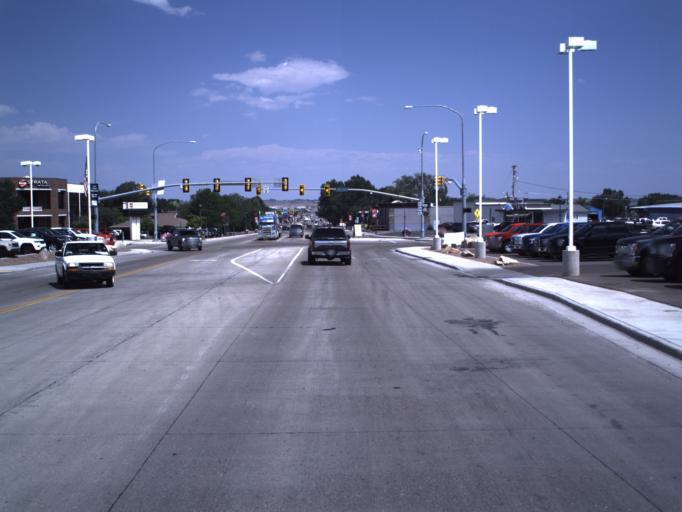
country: US
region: Utah
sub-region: Duchesne County
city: Roosevelt
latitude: 40.3021
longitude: -109.9901
